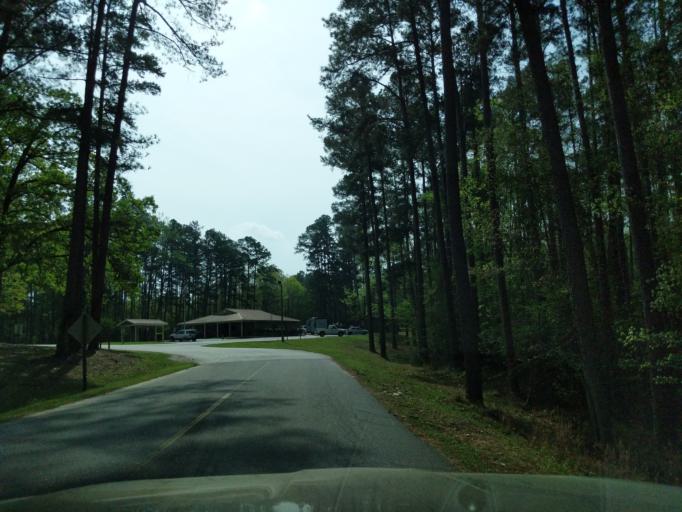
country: US
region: Georgia
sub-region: Lincoln County
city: Lincolnton
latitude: 33.8541
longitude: -82.4046
